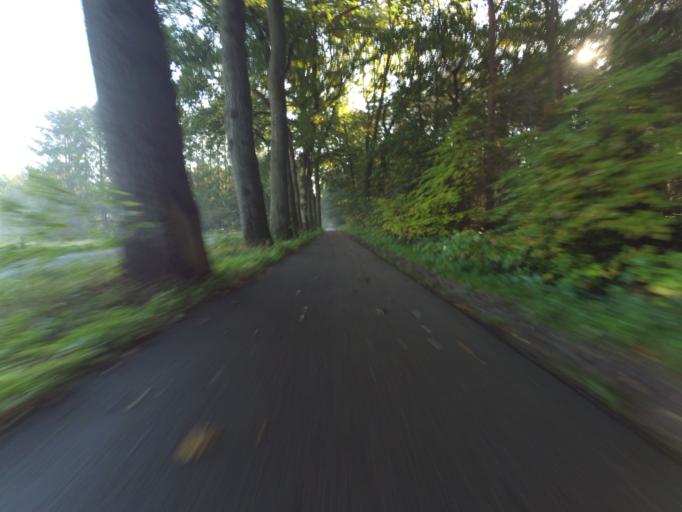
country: NL
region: Gelderland
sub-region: Gemeente Epe
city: Vaassen
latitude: 52.2516
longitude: 5.9270
